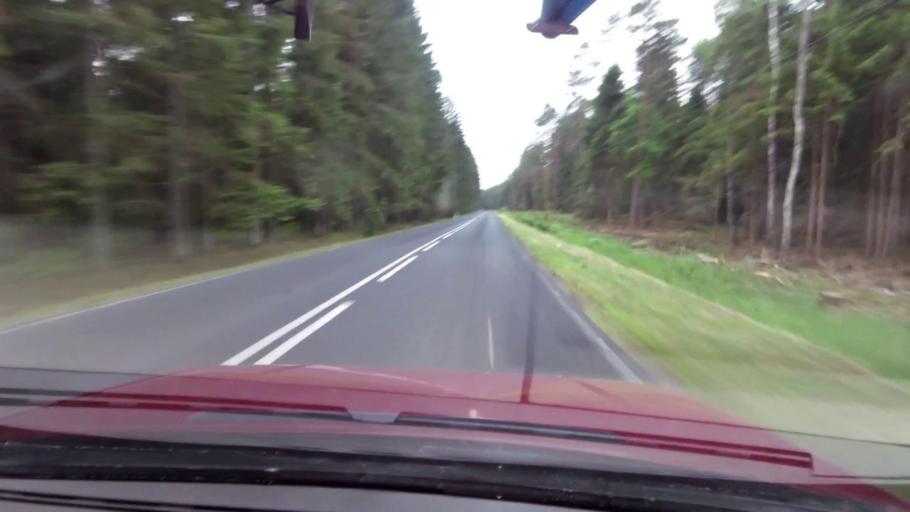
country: PL
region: West Pomeranian Voivodeship
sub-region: Powiat koszalinski
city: Polanow
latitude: 54.1397
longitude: 16.4930
